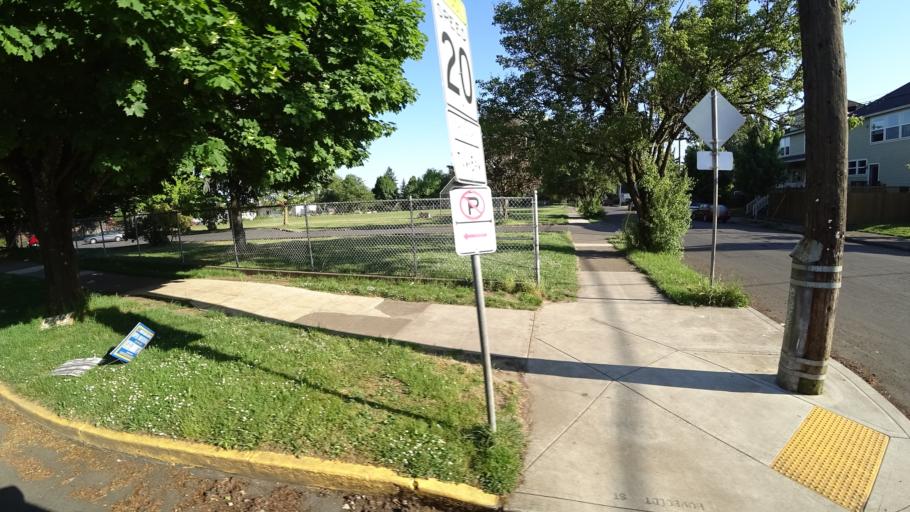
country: US
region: Oregon
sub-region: Multnomah County
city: Portland
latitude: 45.5584
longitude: -122.6873
